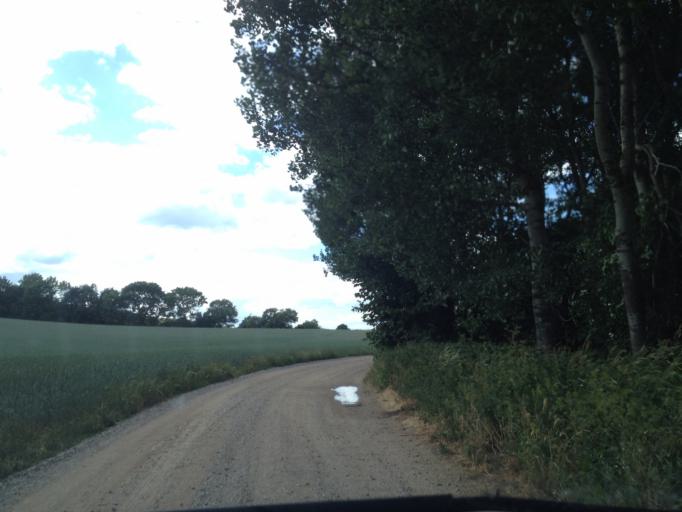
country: DK
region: Central Jutland
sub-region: Syddjurs Kommune
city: Ronde
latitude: 56.1993
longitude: 10.4844
